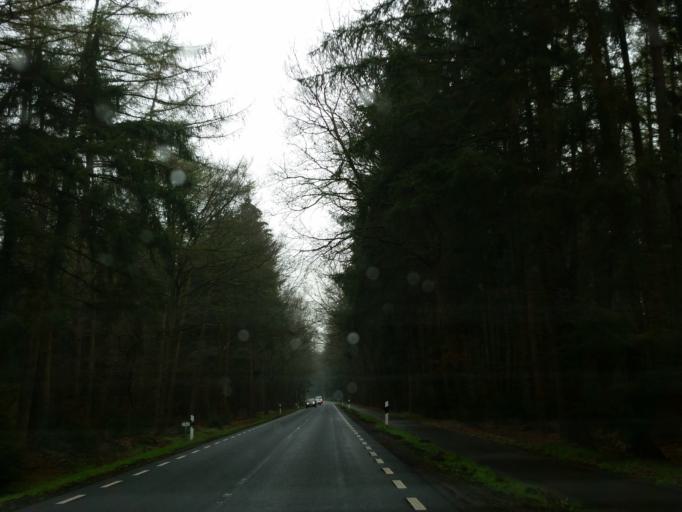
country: DE
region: Lower Saxony
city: Hipstedt
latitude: 53.5179
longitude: 8.9701
